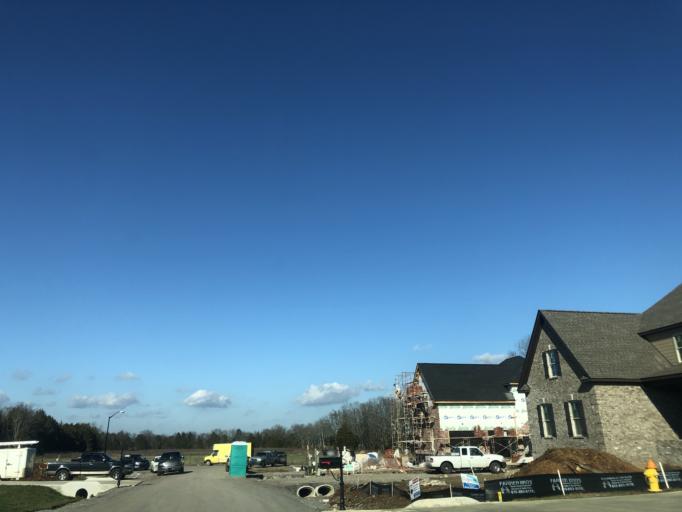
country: US
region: Tennessee
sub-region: Rutherford County
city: Smyrna
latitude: 35.9523
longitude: -86.4173
